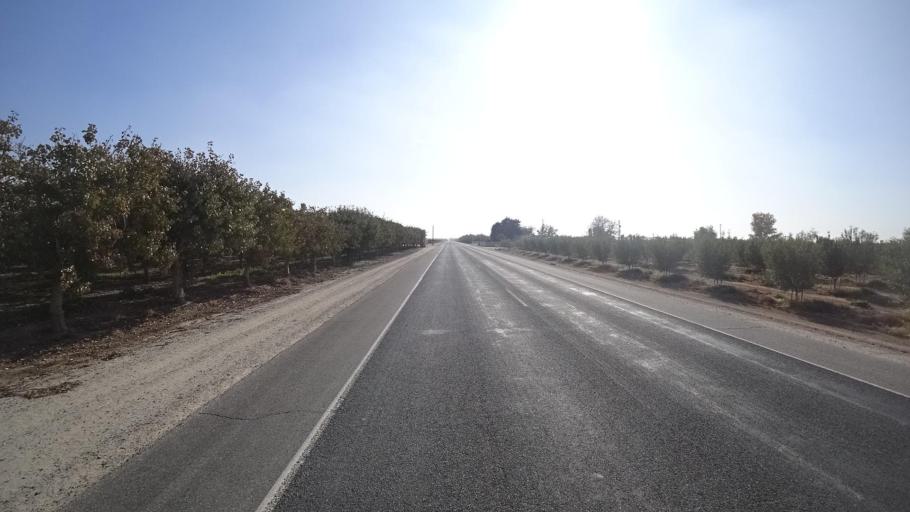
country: US
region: California
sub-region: Kern County
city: McFarland
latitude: 35.6538
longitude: -119.1957
